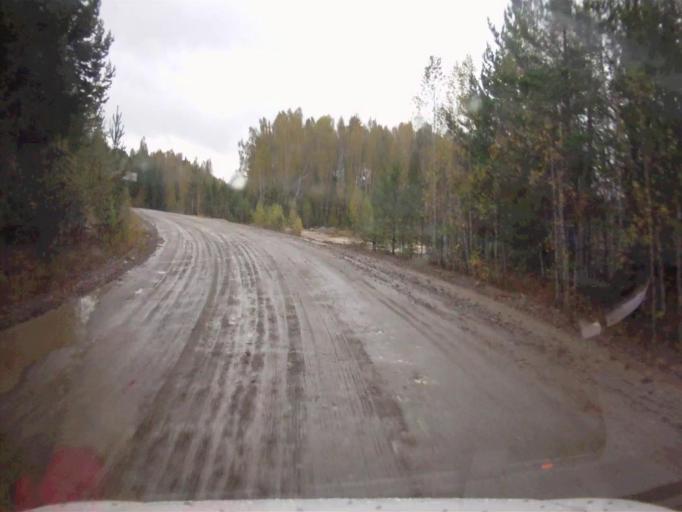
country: RU
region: Chelyabinsk
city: Kyshtym
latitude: 55.8240
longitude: 60.4841
